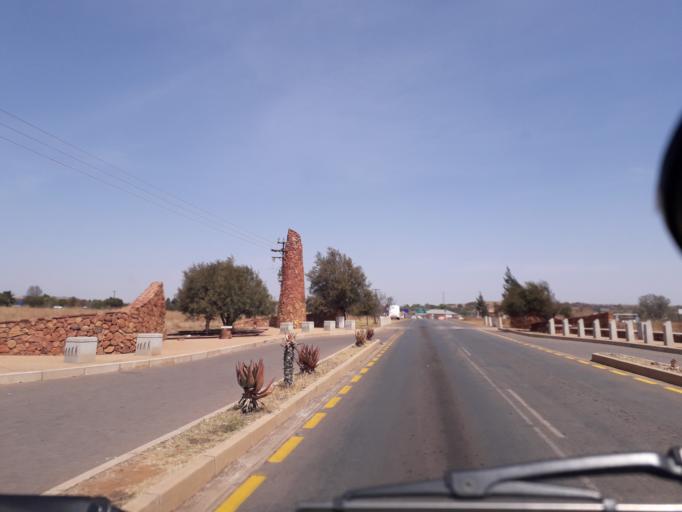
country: ZA
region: Gauteng
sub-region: West Rand District Municipality
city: Krugersdorp
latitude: -26.0215
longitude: 27.7249
